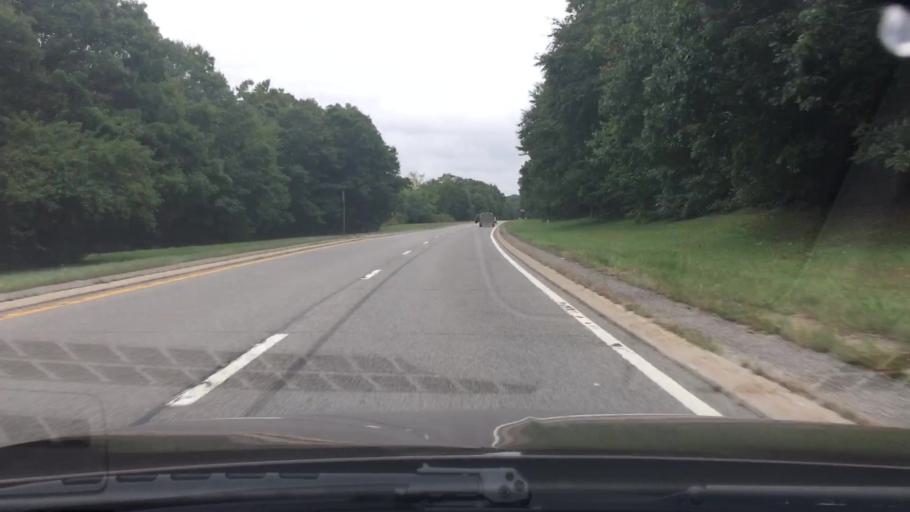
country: US
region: New York
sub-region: Suffolk County
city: Commack
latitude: 40.8253
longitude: -73.3116
